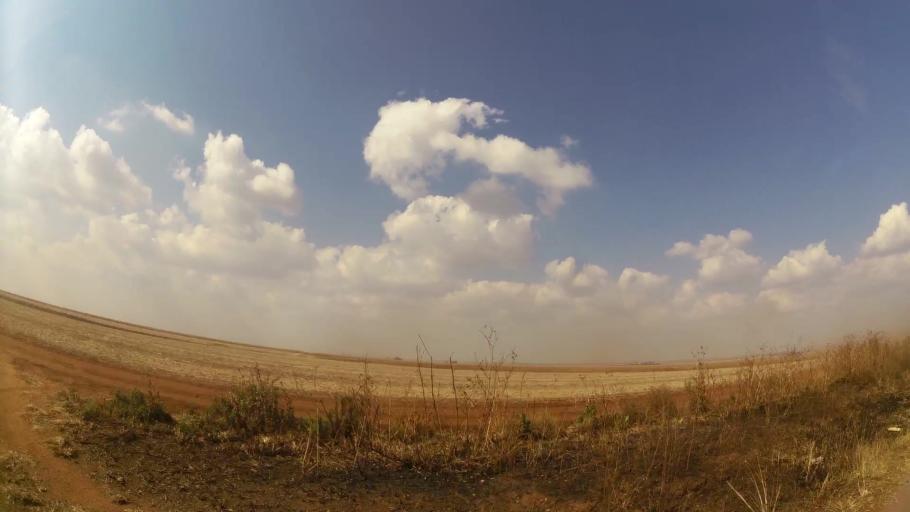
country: ZA
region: Mpumalanga
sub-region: Nkangala District Municipality
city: Delmas
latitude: -26.1981
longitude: 28.5467
